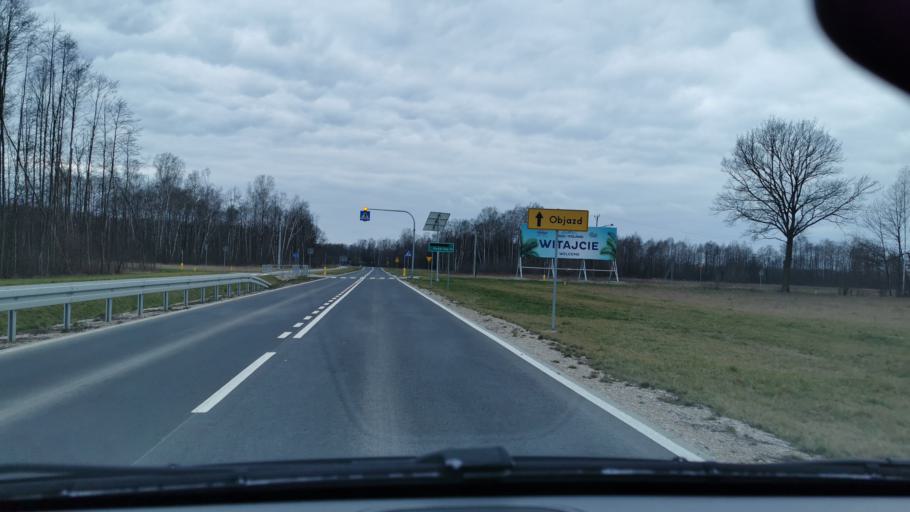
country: PL
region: Masovian Voivodeship
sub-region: Powiat zyrardowski
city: Zyrardow
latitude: 52.0111
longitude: 20.4721
